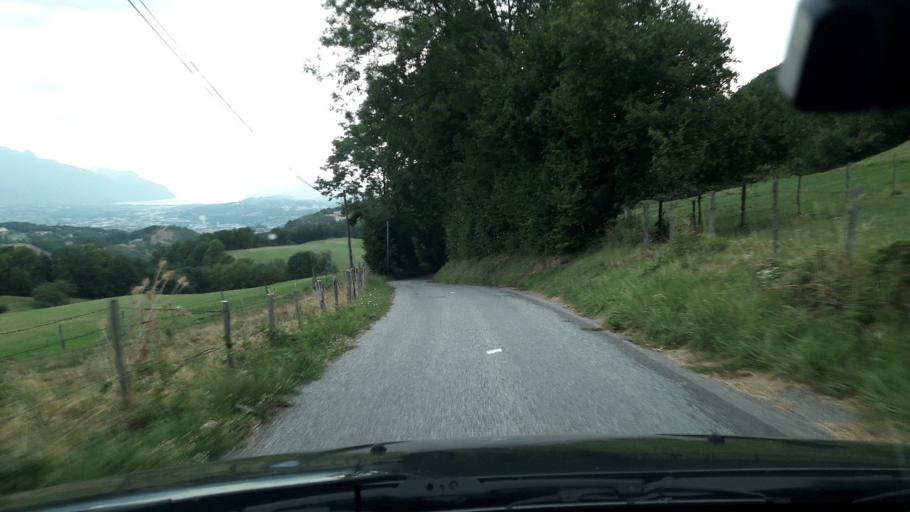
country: FR
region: Rhone-Alpes
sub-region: Departement de la Savoie
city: Saint-Baldoph
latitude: 45.5206
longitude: 5.9238
